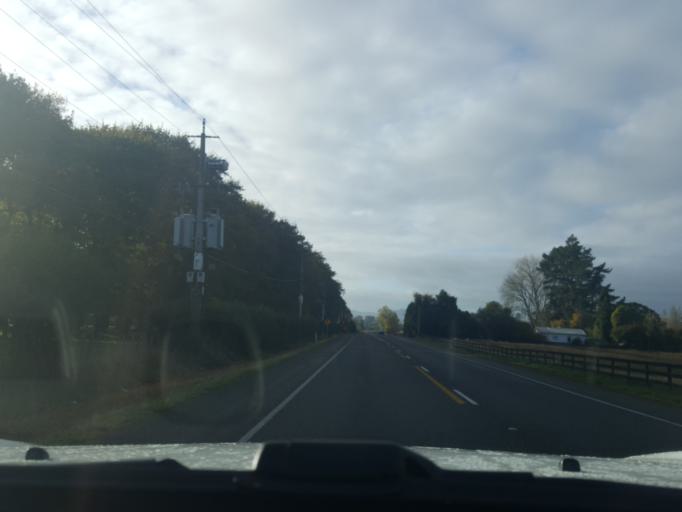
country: NZ
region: Waikato
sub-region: Hamilton City
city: Hamilton
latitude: -37.7776
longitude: 175.3837
